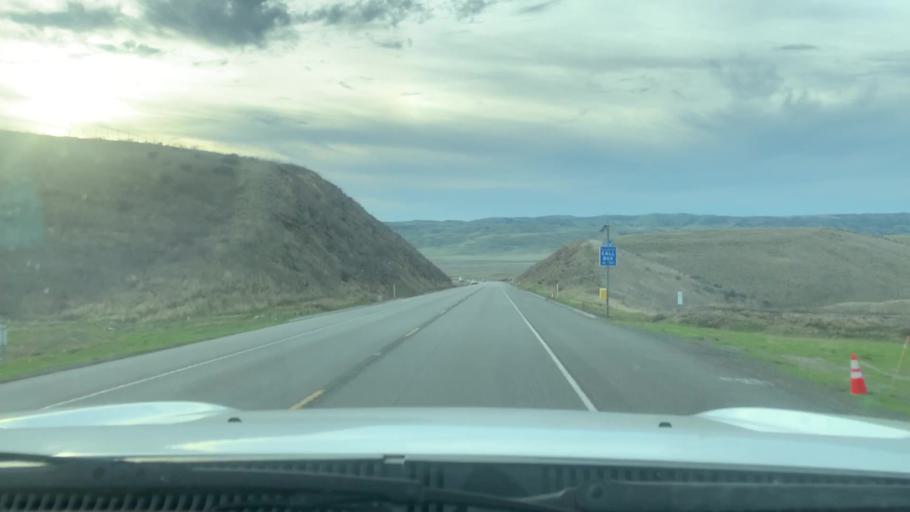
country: US
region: California
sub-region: San Luis Obispo County
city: Shandon
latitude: 35.7417
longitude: -120.2489
